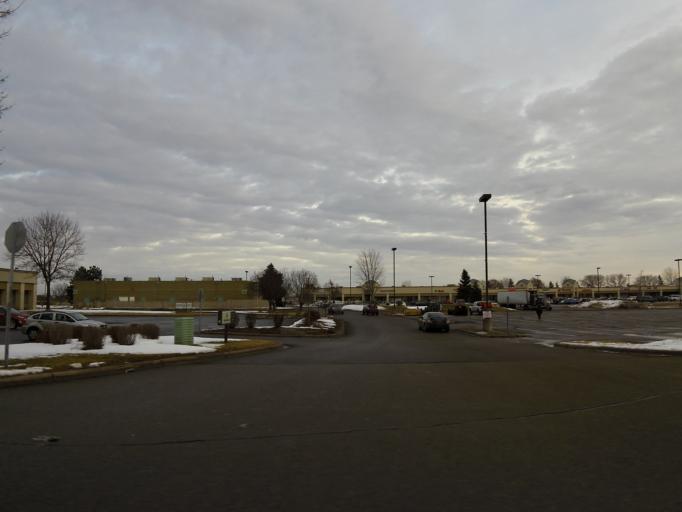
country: US
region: Minnesota
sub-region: Washington County
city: Oakdale
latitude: 44.9618
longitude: -92.9643
